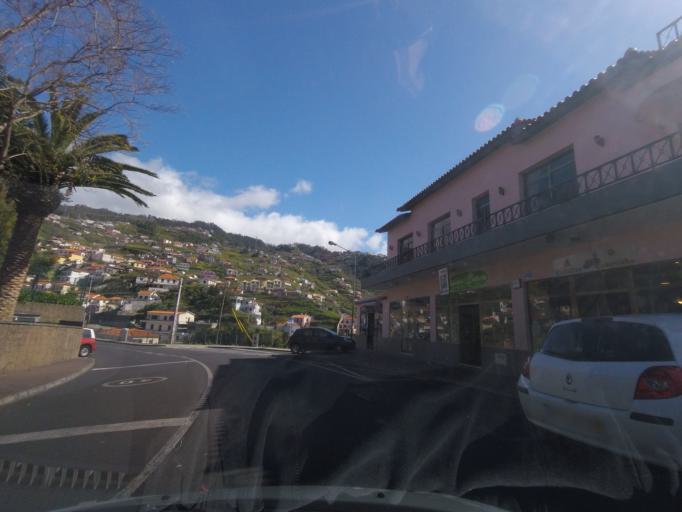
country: PT
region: Madeira
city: Camara de Lobos
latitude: 32.6728
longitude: -16.9780
